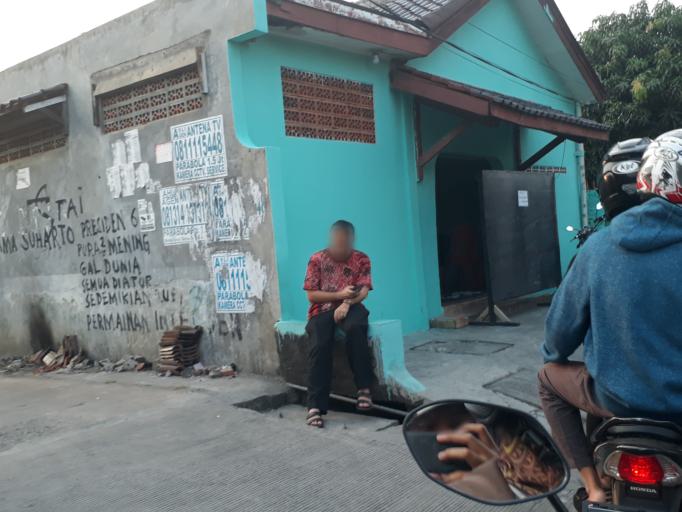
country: ID
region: West Java
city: Bekasi
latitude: -6.2418
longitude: 107.0389
